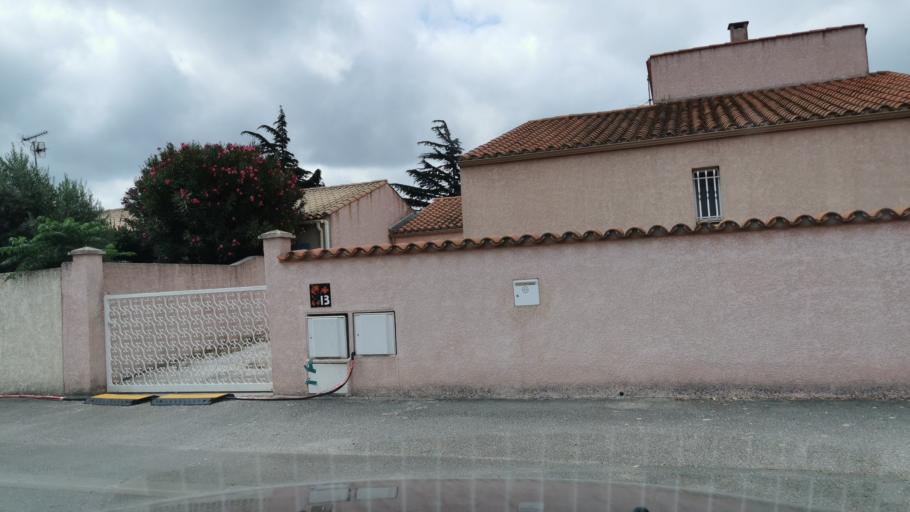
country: FR
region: Languedoc-Roussillon
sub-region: Departement de l'Aude
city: Narbonne
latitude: 43.1884
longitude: 3.0290
